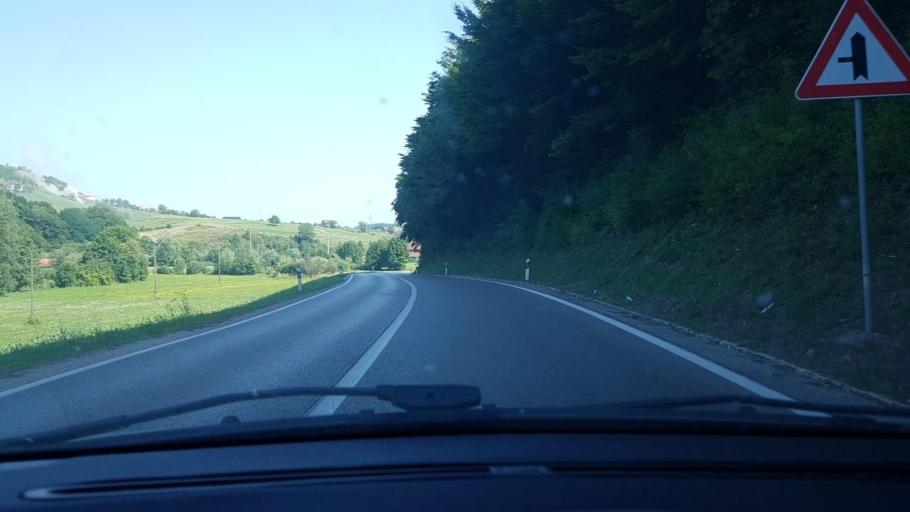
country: BA
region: Federation of Bosnia and Herzegovina
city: Mala Kladusa
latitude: 45.1190
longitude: 15.8647
